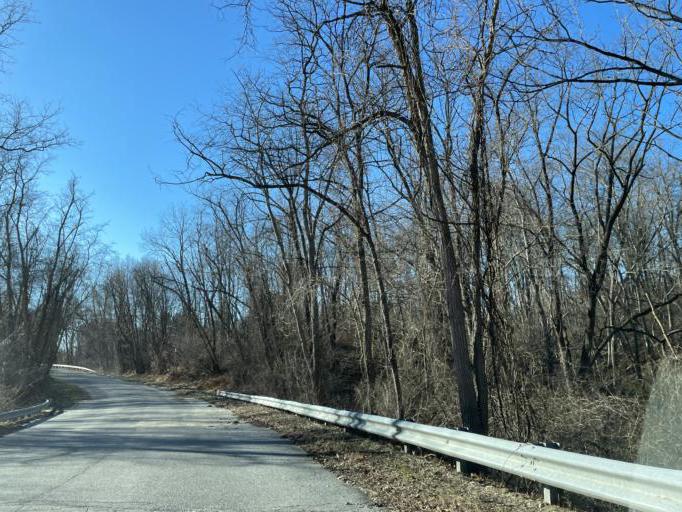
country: US
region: Pennsylvania
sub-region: York County
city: New Freedom
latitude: 39.6614
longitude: -76.6483
